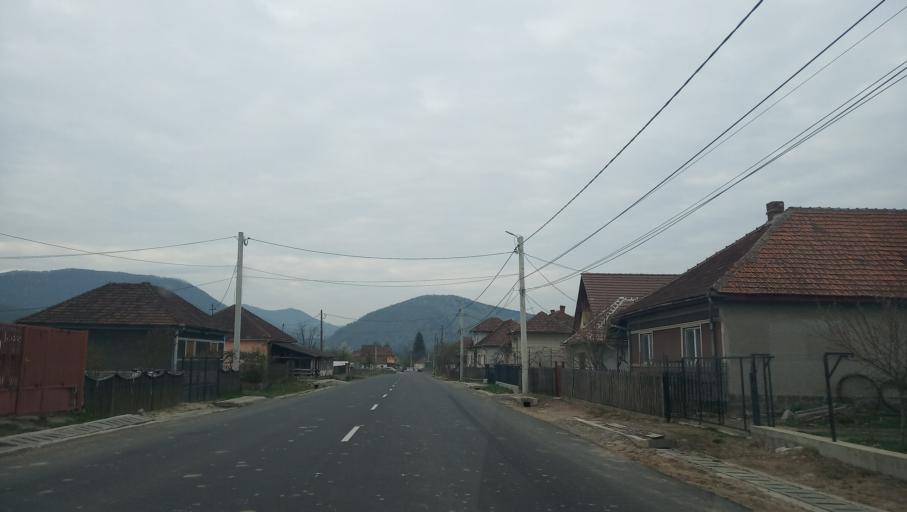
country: RO
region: Arad
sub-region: Comuna Varfurile
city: Varfurile
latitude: 46.3091
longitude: 22.5296
